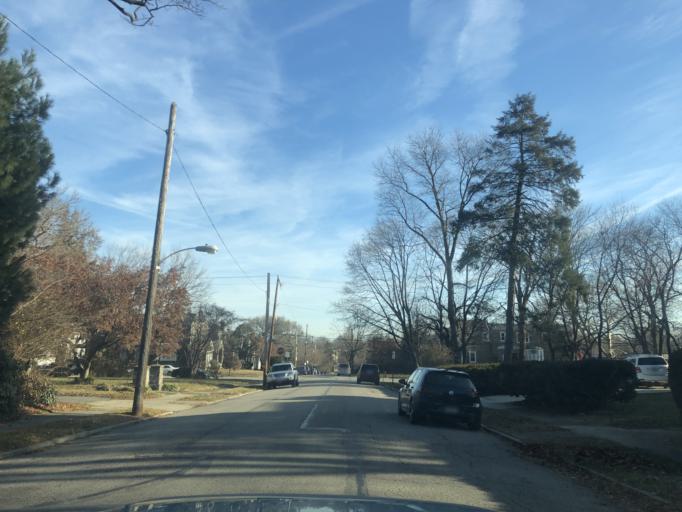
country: US
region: Pennsylvania
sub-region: Montgomery County
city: Bala-Cynwyd
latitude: 39.9900
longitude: -75.2415
